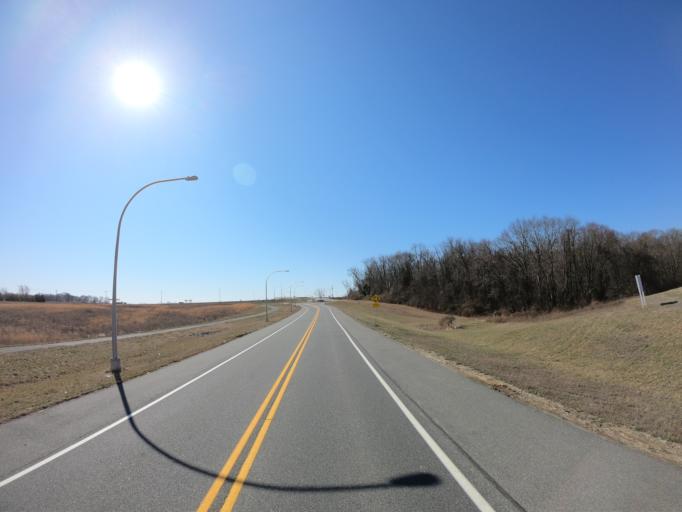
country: US
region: Delaware
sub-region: New Castle County
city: Middletown
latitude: 39.5287
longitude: -75.6788
